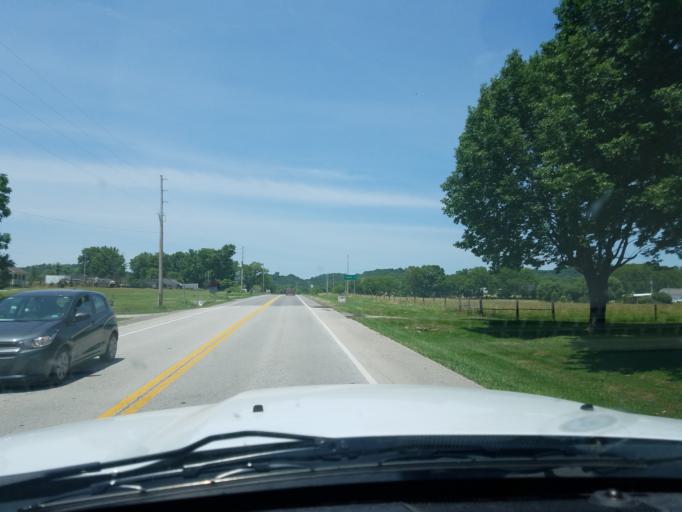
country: US
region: Tennessee
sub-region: Sumner County
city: Westmoreland
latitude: 36.4526
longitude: -86.2671
